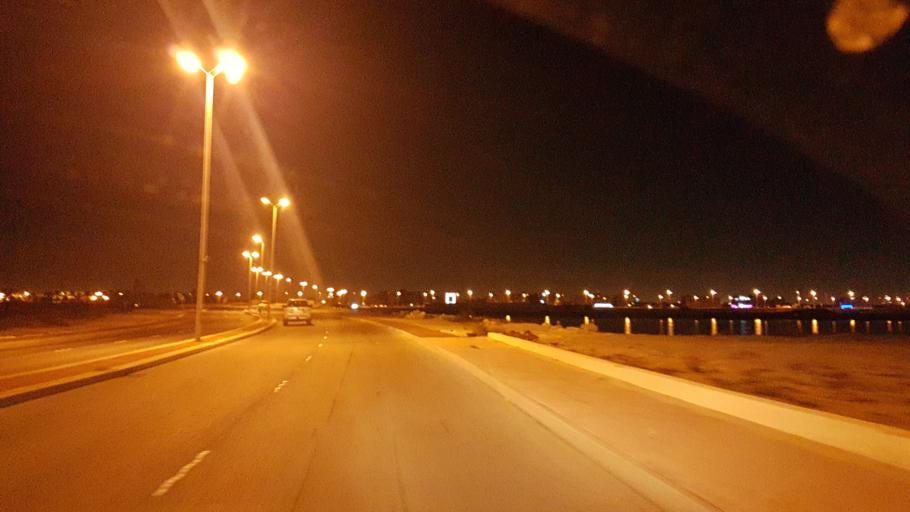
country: BH
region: Muharraq
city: Al Hadd
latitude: 26.2863
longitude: 50.6595
